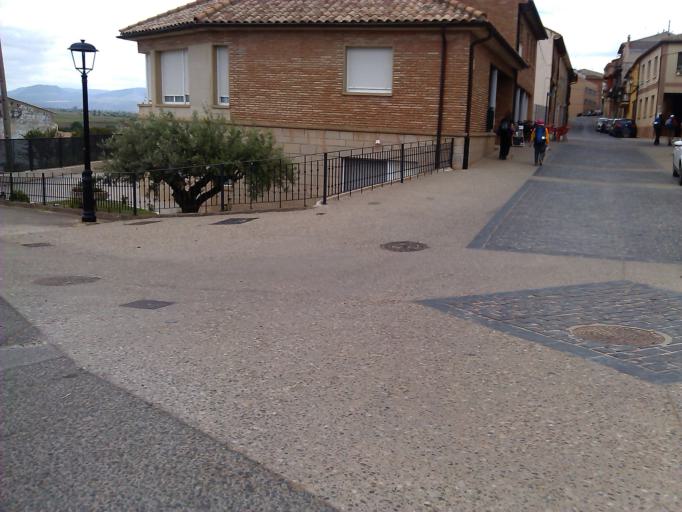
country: ES
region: La Rioja
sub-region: Provincia de La Rioja
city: Navarrete
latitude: 42.4323
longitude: -2.5593
